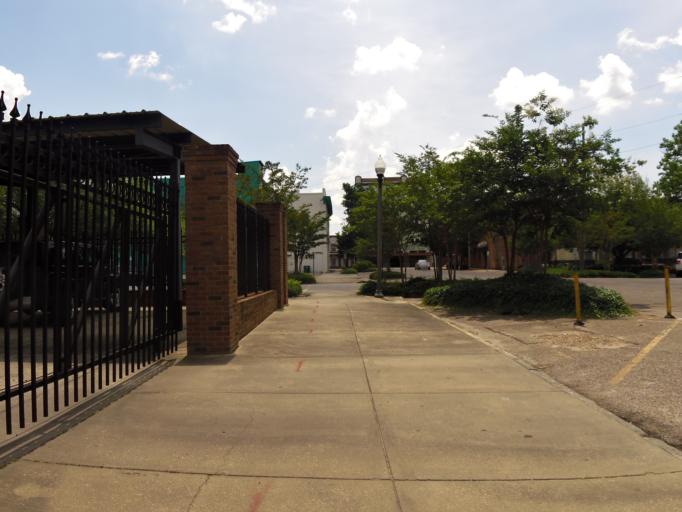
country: US
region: Mississippi
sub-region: Lauderdale County
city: Meridian
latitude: 32.3630
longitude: -88.7005
